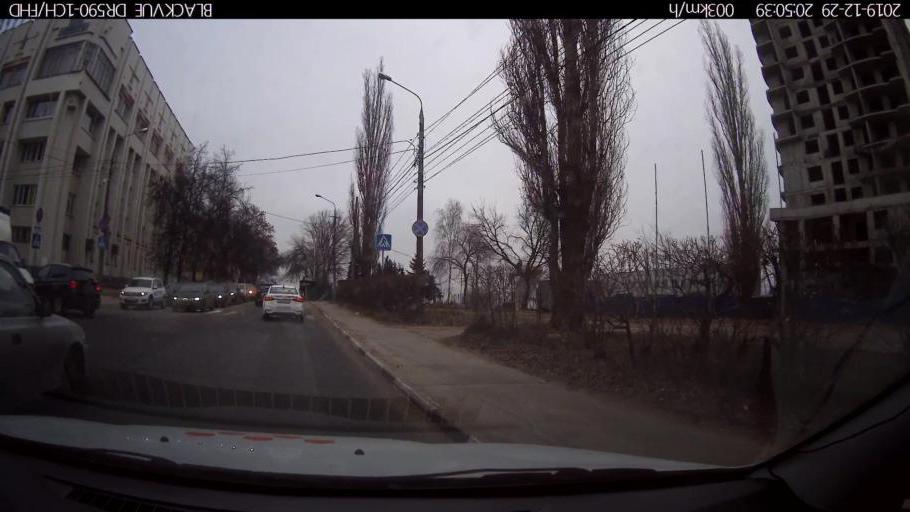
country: RU
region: Nizjnij Novgorod
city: Nizhniy Novgorod
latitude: 56.3194
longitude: 44.0328
